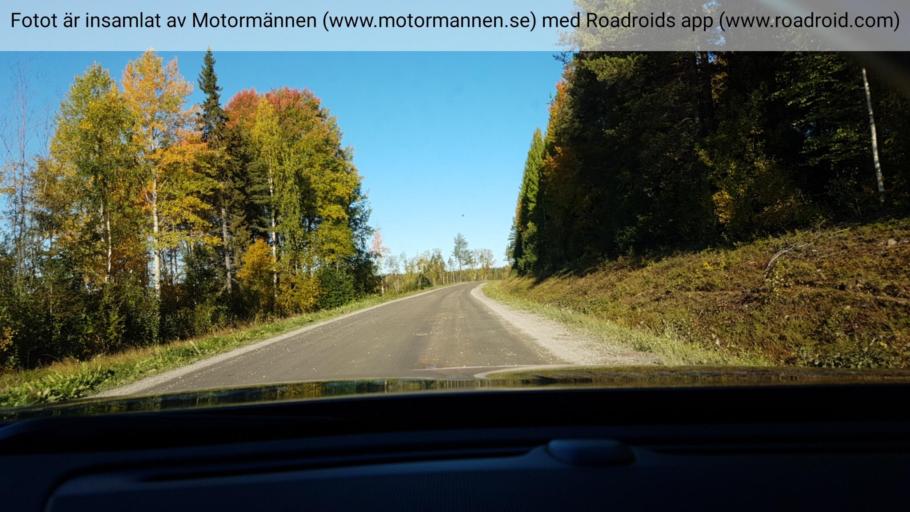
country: SE
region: Norrbotten
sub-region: Alvsbyns Kommun
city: AElvsbyn
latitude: 66.1882
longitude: 21.2025
